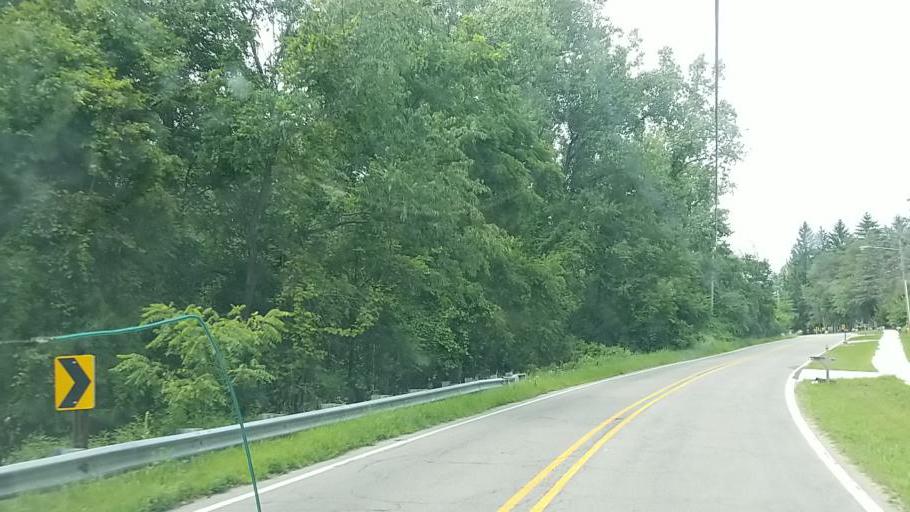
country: US
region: Michigan
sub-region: Kent County
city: Walker
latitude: 42.9994
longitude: -85.7363
